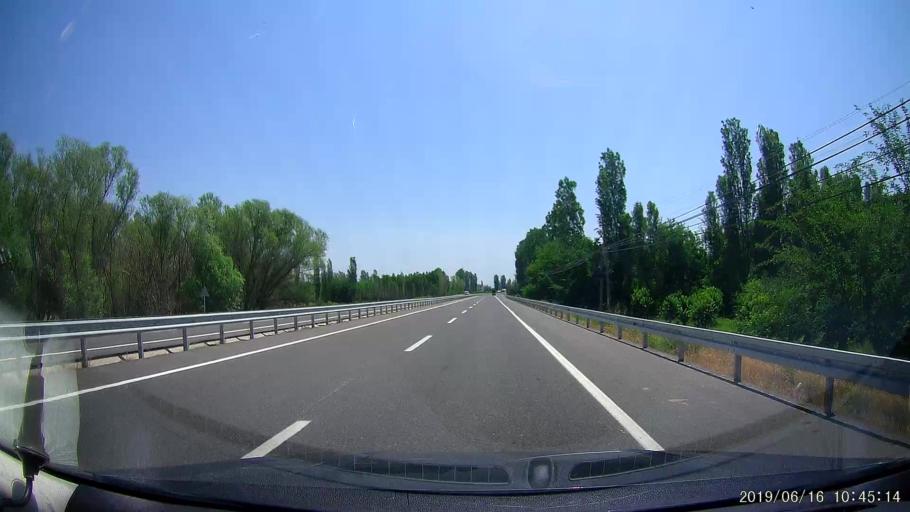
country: AM
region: Armavir
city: Shenavan
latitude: 40.0279
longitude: 43.8664
